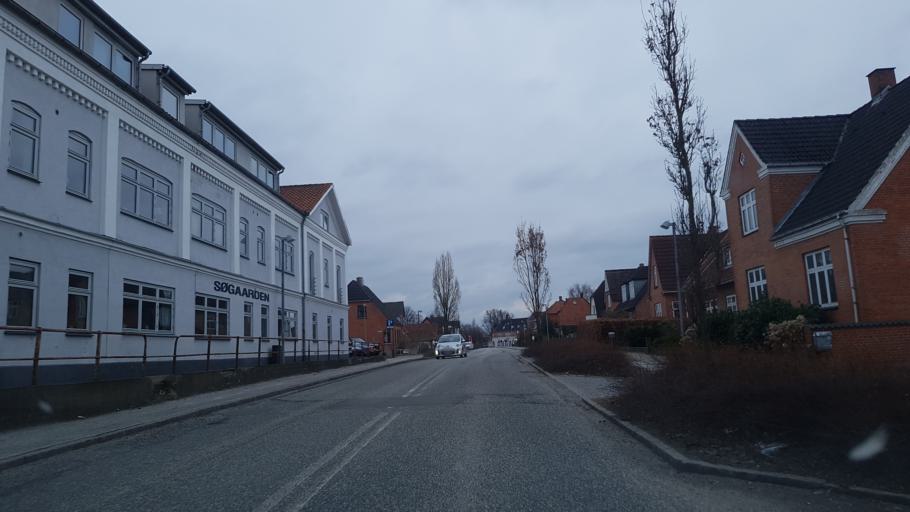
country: DK
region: Zealand
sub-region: Soro Kommune
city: Soro
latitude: 55.4416
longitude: 11.5599
